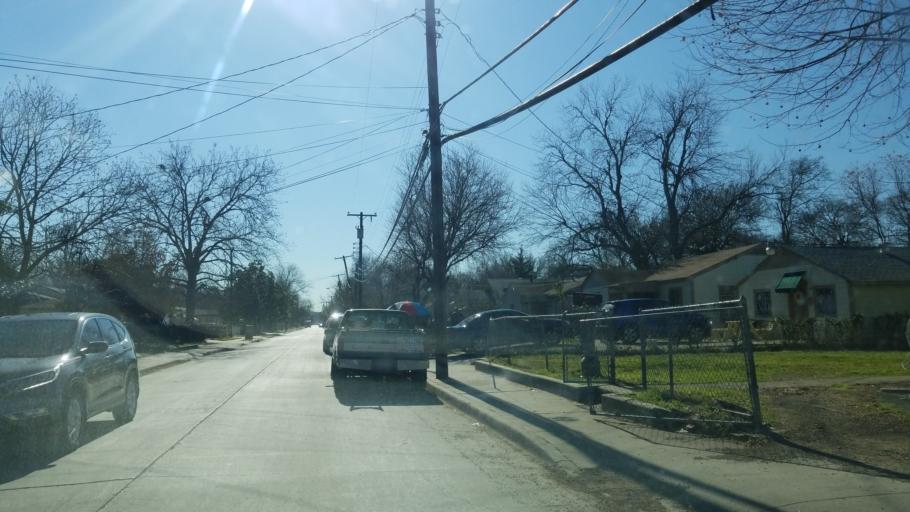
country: US
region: Texas
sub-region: Dallas County
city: Cockrell Hill
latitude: 32.7560
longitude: -96.9128
